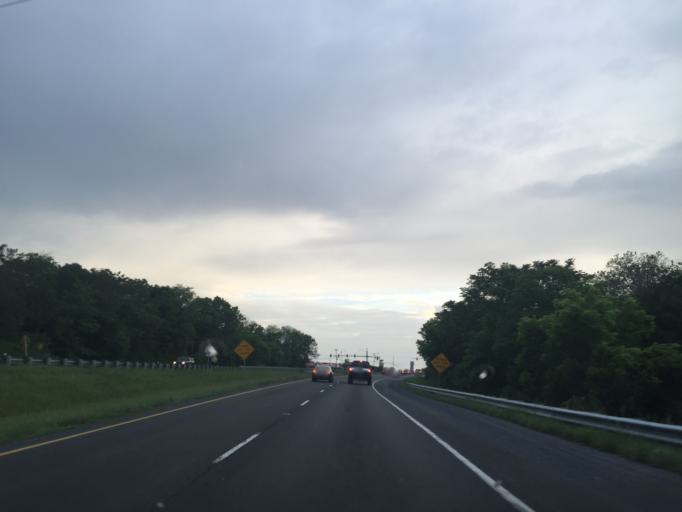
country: US
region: Virginia
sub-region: City of Winchester
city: Winchester
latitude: 39.1881
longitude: -78.1165
